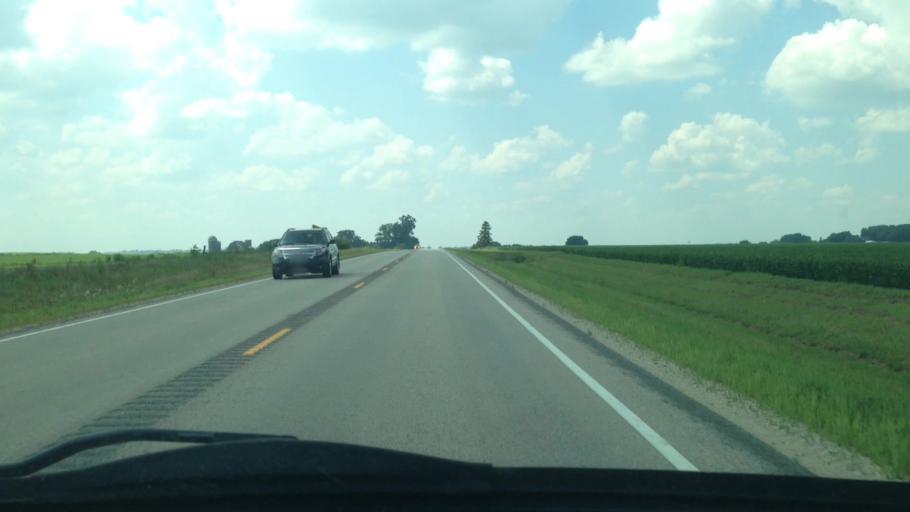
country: US
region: Minnesota
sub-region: Olmsted County
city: Stewartville
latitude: 43.8555
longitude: -92.4231
